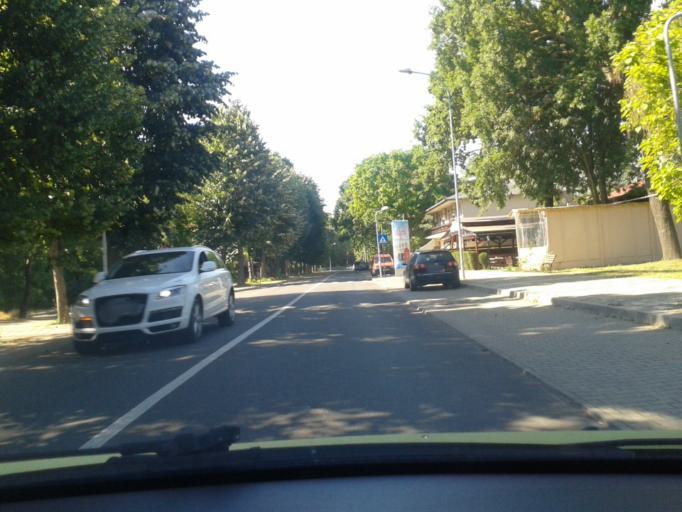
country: RO
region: Constanta
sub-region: Comuna Douazeci si Trei August
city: Douazeci si Trei August
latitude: 43.8774
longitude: 28.6030
